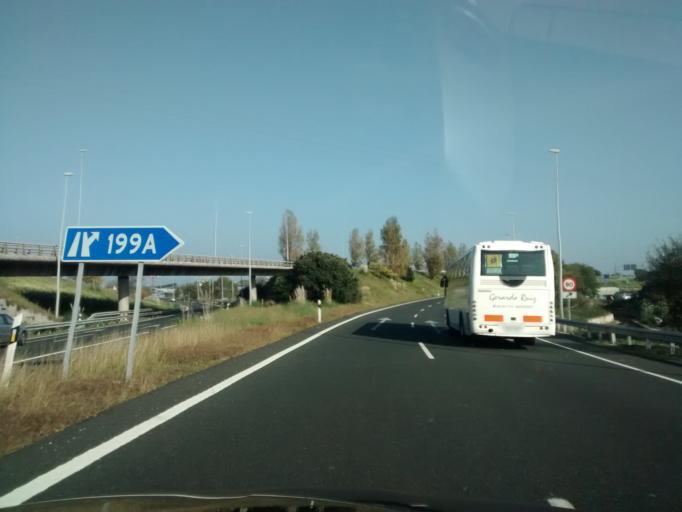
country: ES
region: Cantabria
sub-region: Provincia de Cantabria
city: Santa Cruz de Bezana
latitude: 43.4396
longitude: -3.8950
